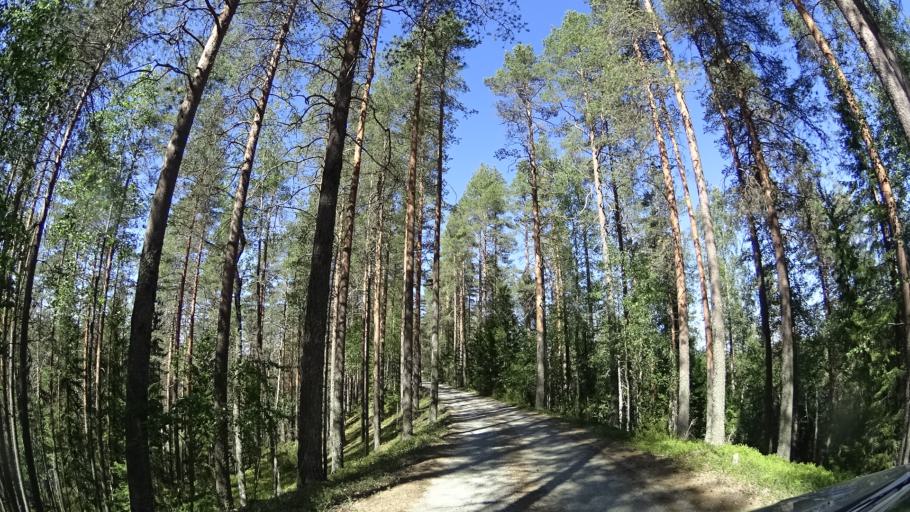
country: FI
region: Kainuu
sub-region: Kajaani
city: Vuolijoki
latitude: 63.9745
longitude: 26.7993
